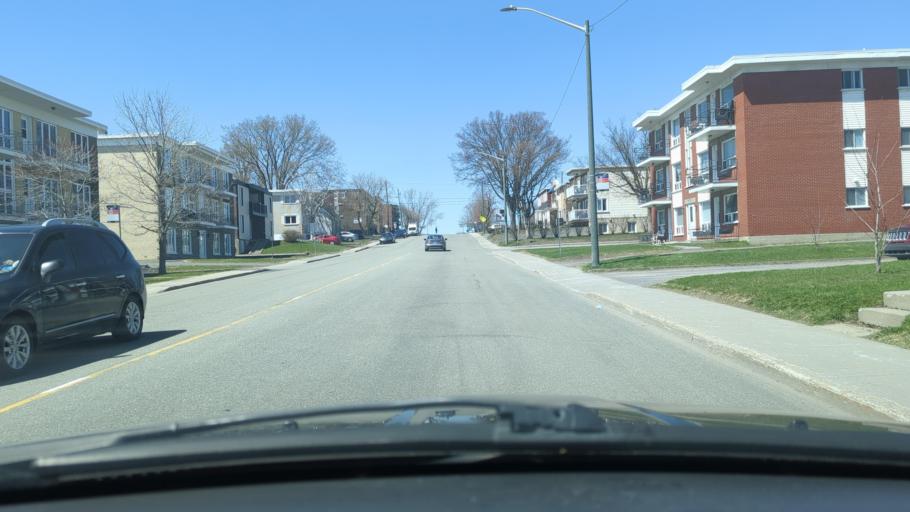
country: CA
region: Quebec
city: Quebec
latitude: 46.8579
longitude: -71.2088
